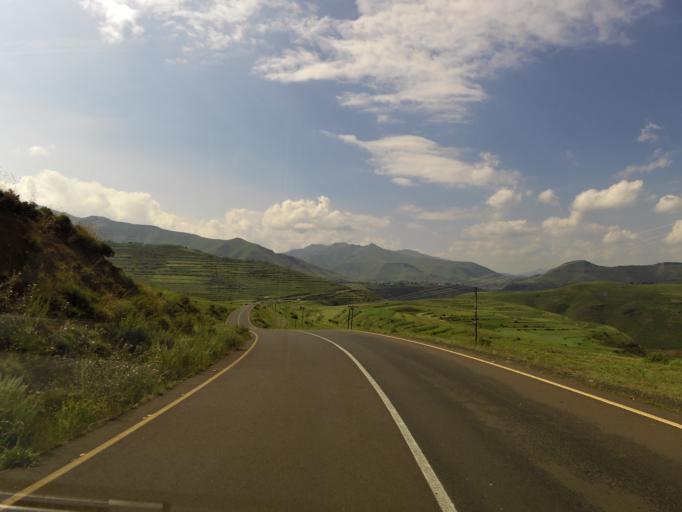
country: LS
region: Thaba-Tseka
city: Thaba-Tseka
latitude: -29.1334
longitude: 28.4934
